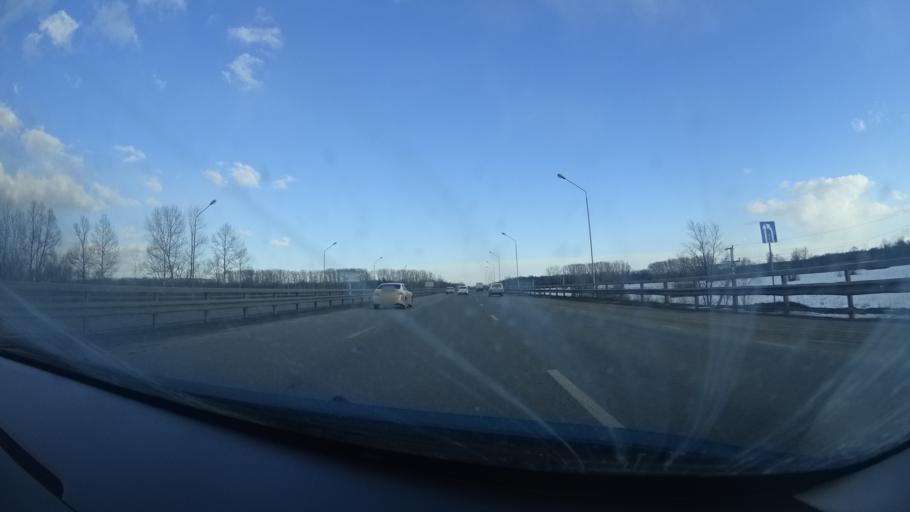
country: RU
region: Bashkortostan
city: Ufa
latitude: 54.6574
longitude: 55.8914
